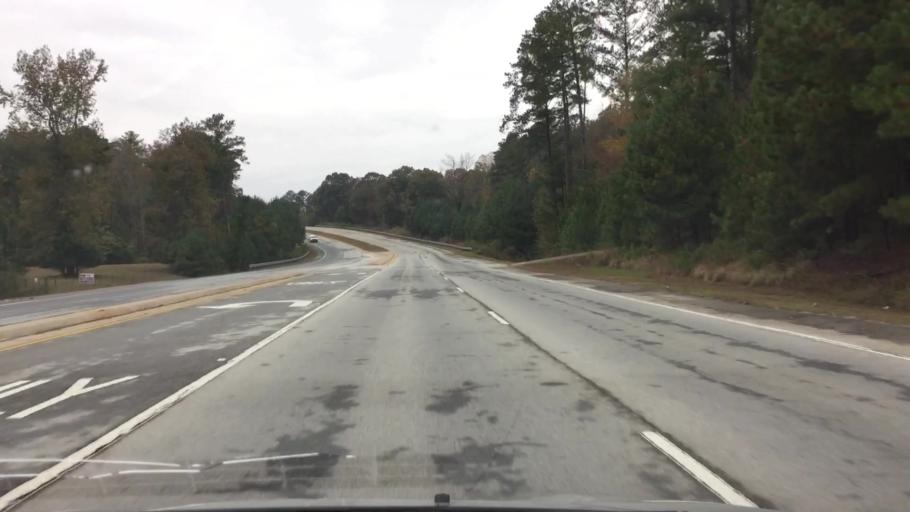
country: US
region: Georgia
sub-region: Henry County
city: Stockbridge
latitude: 33.5206
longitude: -84.1793
